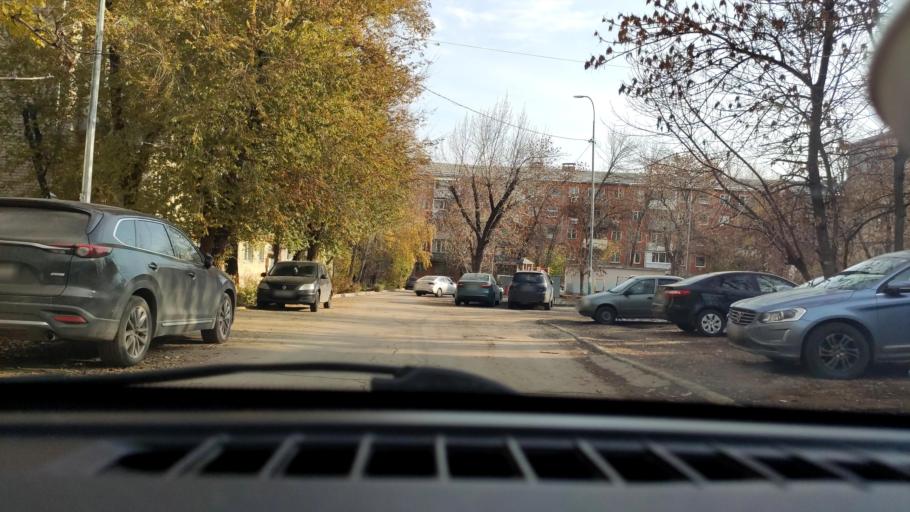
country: RU
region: Samara
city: Samara
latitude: 53.1960
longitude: 50.2071
